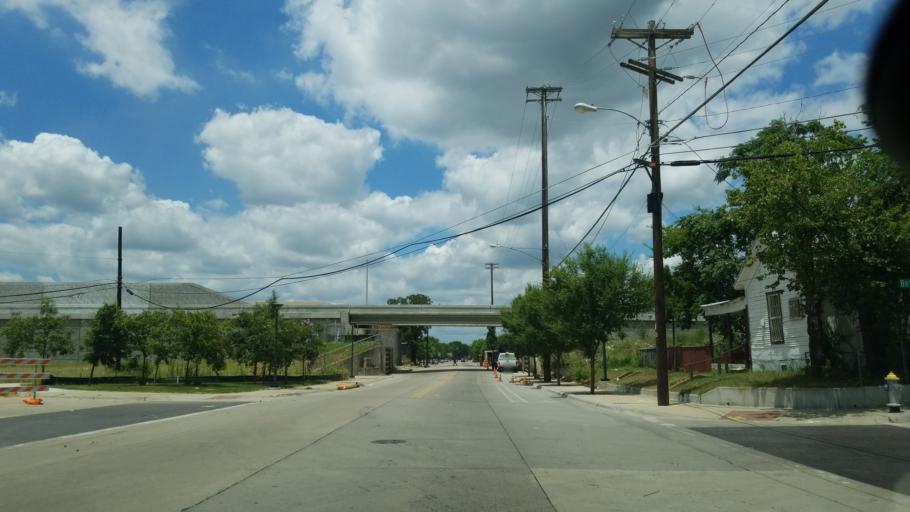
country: US
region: Texas
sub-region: Dallas County
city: Dallas
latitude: 32.7462
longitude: -96.7534
